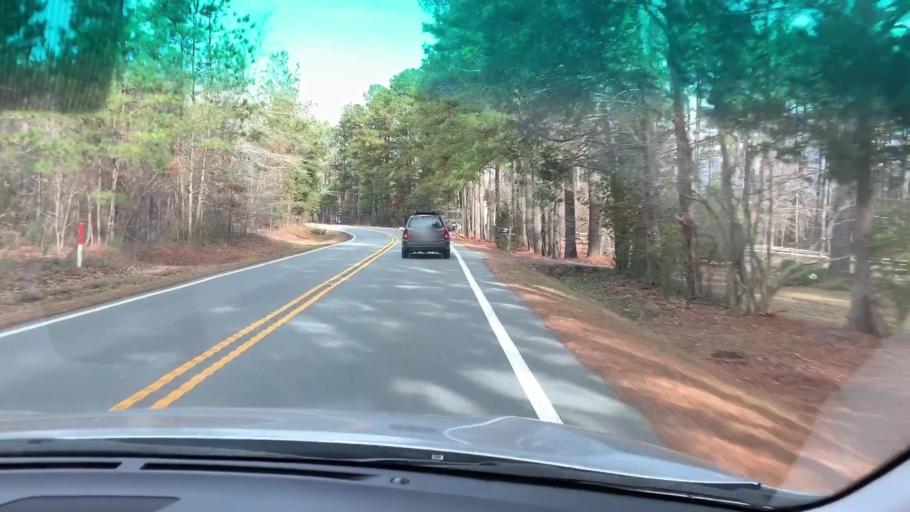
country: US
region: North Carolina
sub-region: Wake County
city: Green Level
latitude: 35.8606
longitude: -78.9414
